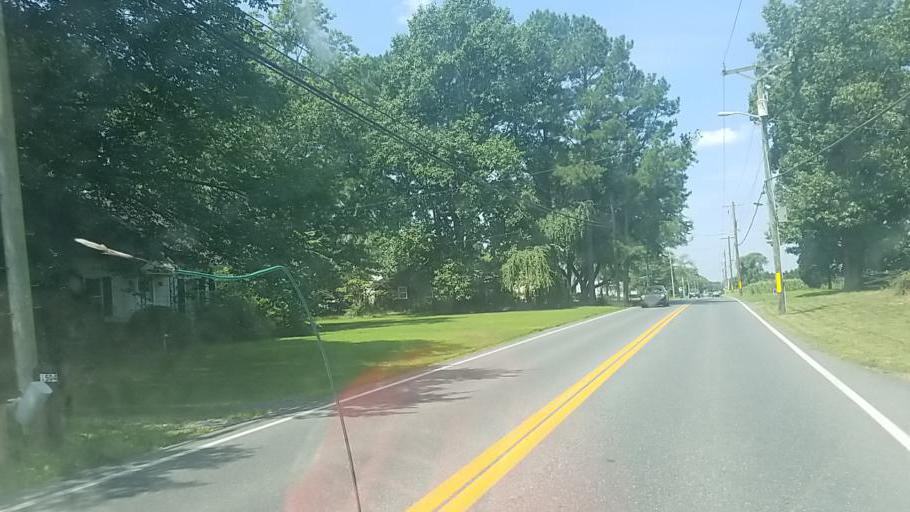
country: US
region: Maryland
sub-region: Wicomico County
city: Salisbury
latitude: 38.3632
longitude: -75.5590
